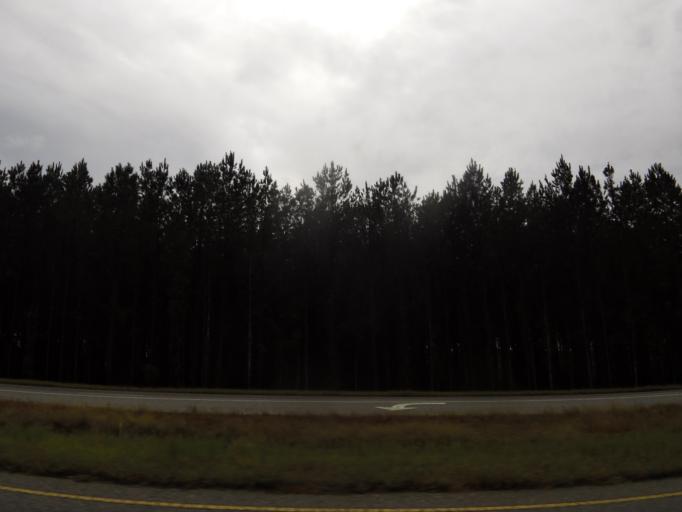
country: US
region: Georgia
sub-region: Wayne County
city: Jesup
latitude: 31.5256
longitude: -81.7840
